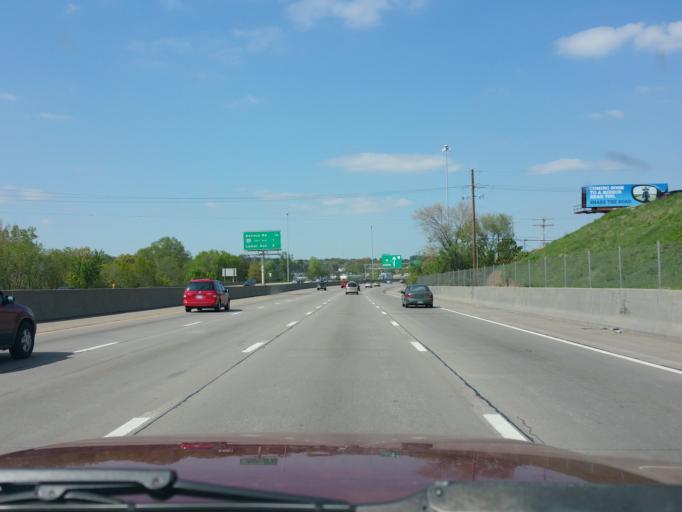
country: US
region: Kansas
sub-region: Johnson County
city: Merriam
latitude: 39.0288
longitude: -94.6898
